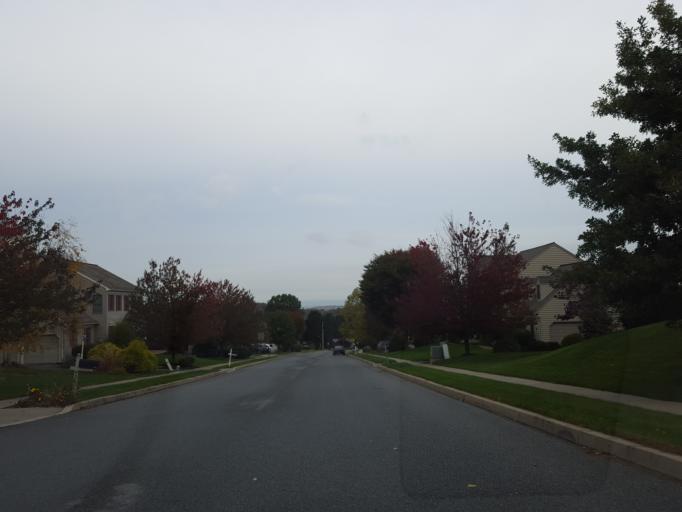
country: US
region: Pennsylvania
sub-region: York County
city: Spry
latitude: 39.9273
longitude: -76.6627
